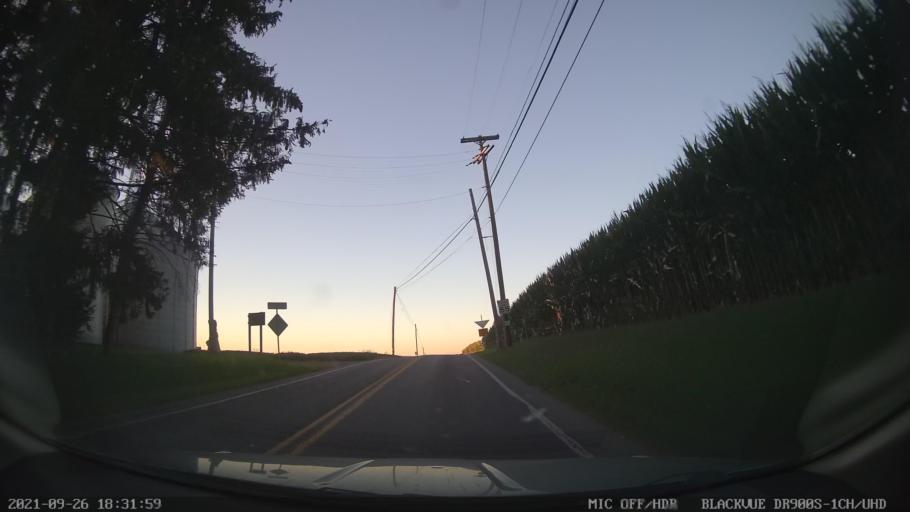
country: US
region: Pennsylvania
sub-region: Berks County
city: Kutztown
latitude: 40.4843
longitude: -75.7585
